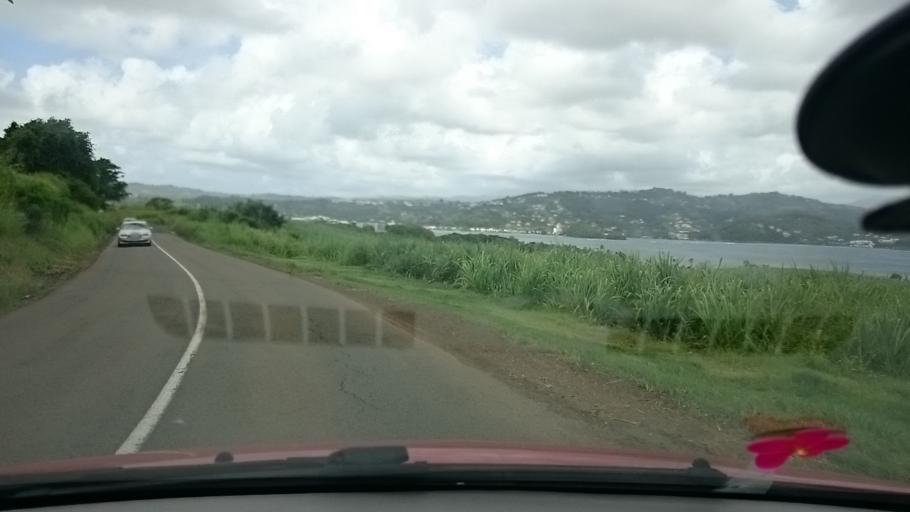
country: MQ
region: Martinique
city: Petite Riviere Salee
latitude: 14.7518
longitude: -60.9426
